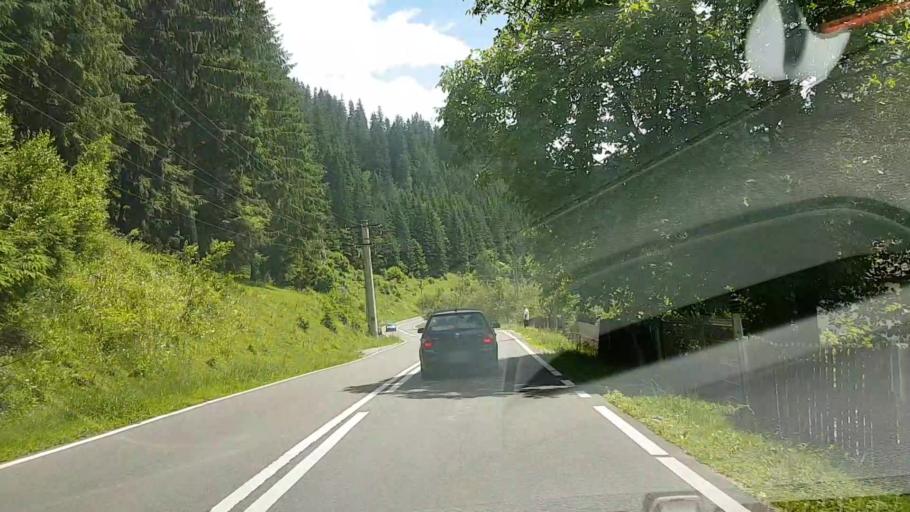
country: RO
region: Suceava
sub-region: Comuna Brosteni
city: Brosteni
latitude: 47.2701
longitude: 25.6526
